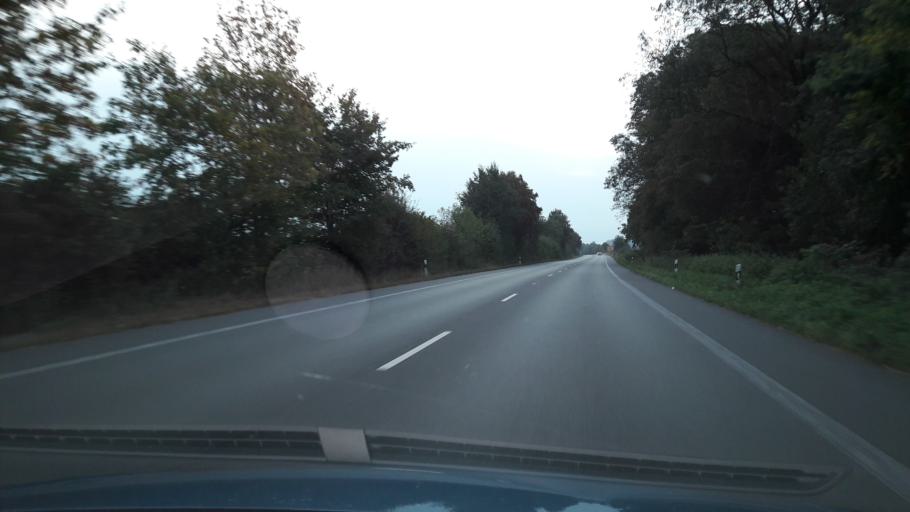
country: DE
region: North Rhine-Westphalia
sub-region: Regierungsbezirk Munster
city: Everswinkel
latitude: 51.9291
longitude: 7.8209
